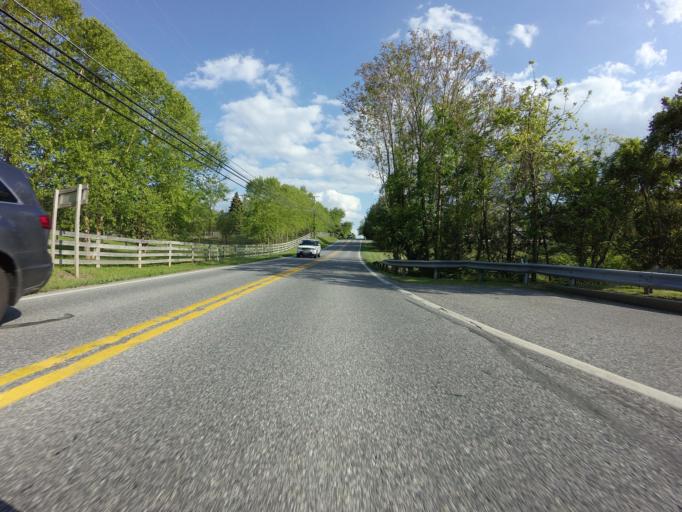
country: US
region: Maryland
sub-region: Baltimore County
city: Cockeysville
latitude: 39.4740
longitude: -76.7050
